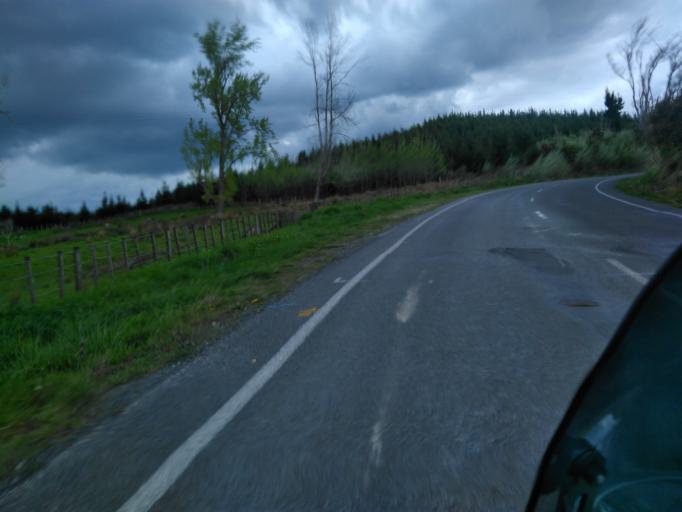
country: NZ
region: Gisborne
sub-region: Gisborne District
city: Gisborne
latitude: -38.6785
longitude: 177.8018
